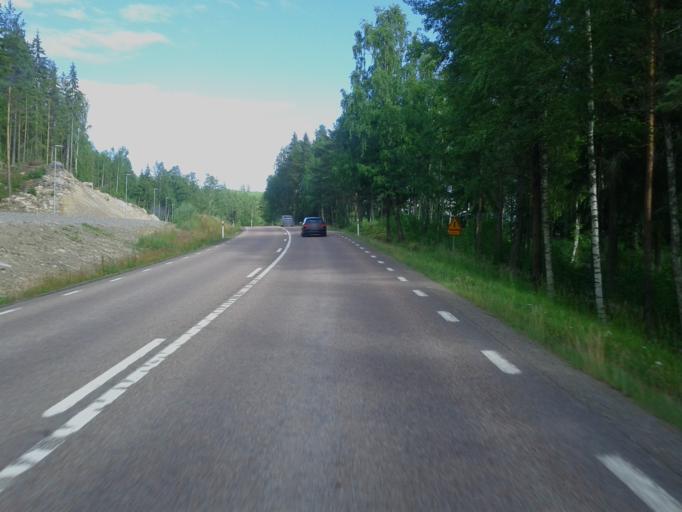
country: SE
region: Dalarna
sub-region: Faluns Kommun
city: Grycksbo
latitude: 60.6711
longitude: 15.5245
